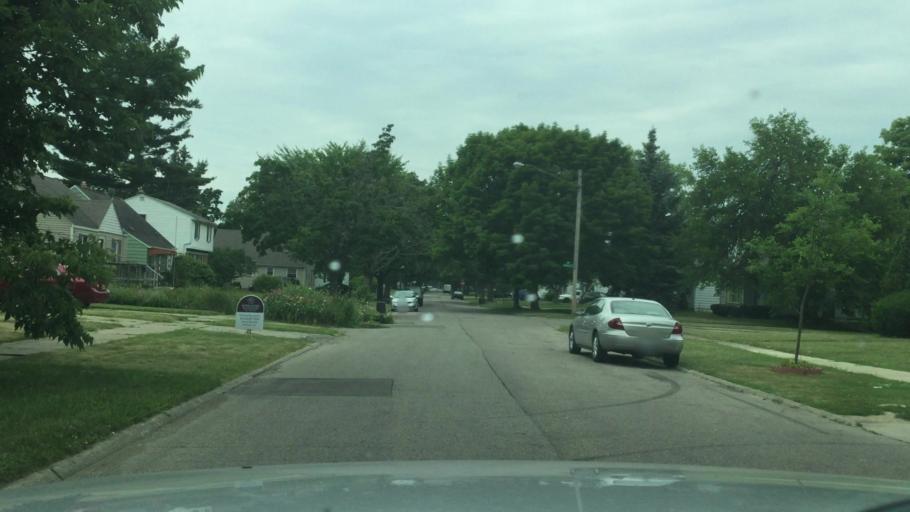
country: US
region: Michigan
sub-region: Genesee County
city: Flint
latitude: 43.0248
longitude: -83.6589
